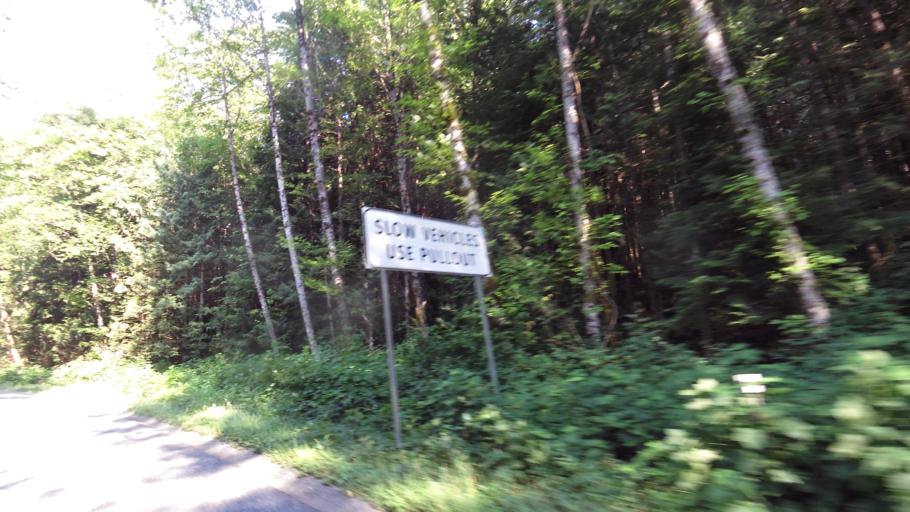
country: CA
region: British Columbia
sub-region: Regional District of Alberni-Clayoquot
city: Ucluelet
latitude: 49.0823
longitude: -125.4578
